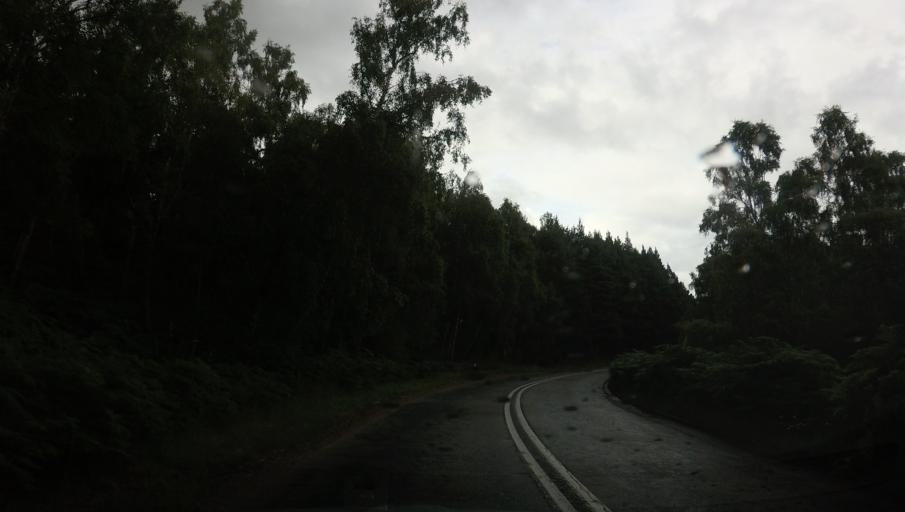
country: GB
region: Scotland
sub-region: Aberdeenshire
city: Ballater
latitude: 57.0583
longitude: -3.1250
